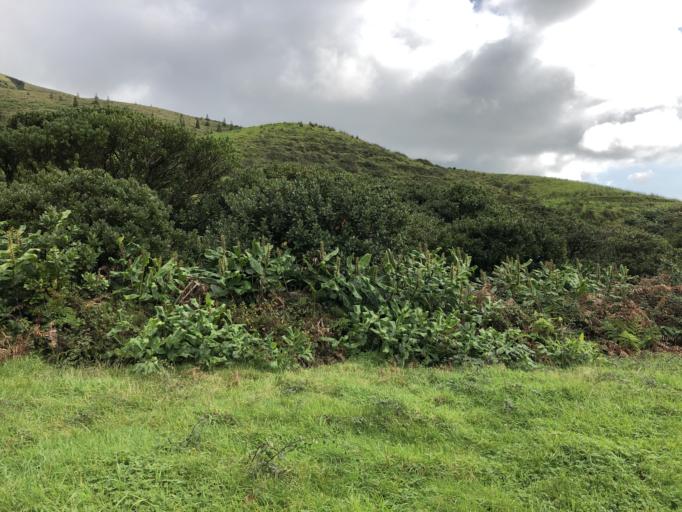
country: PT
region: Azores
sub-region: Ponta Delgada
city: Arrifes
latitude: 37.8286
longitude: -25.7645
